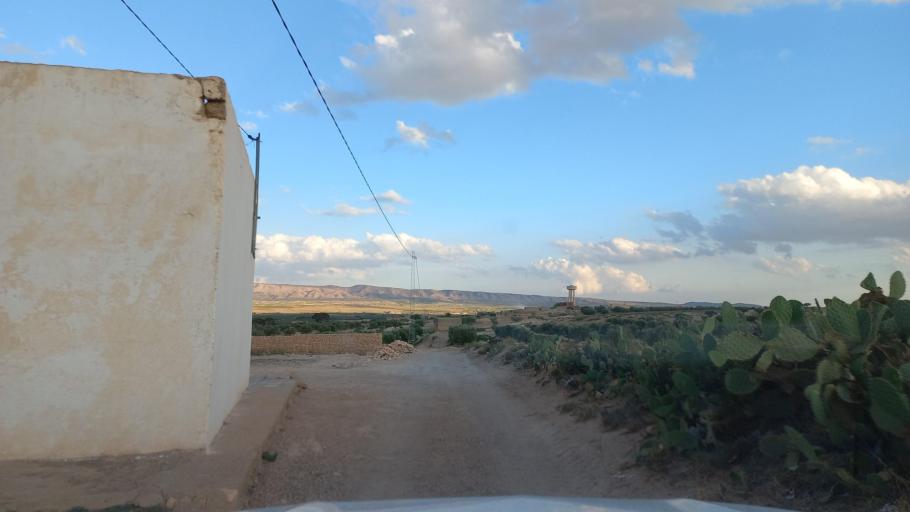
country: TN
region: Al Qasrayn
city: Sbiba
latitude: 35.3761
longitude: 9.0579
